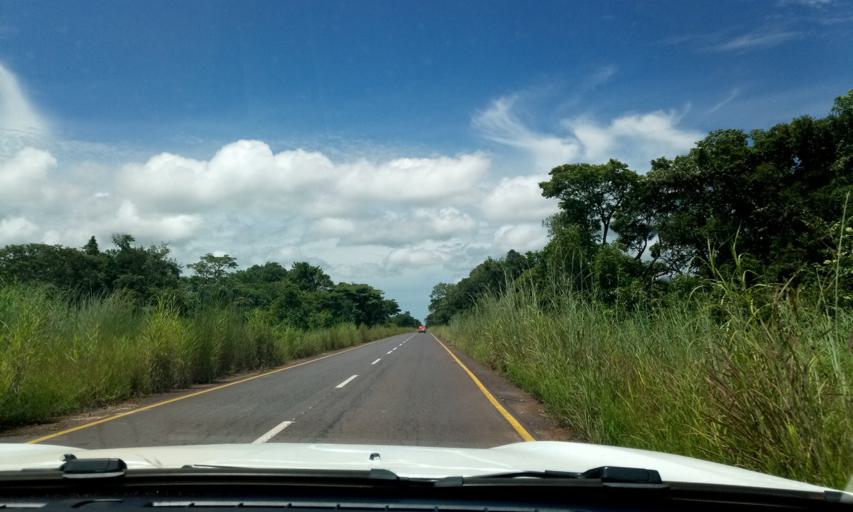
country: CD
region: Katanga
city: Lubumbashi
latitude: -11.1038
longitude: 27.9769
